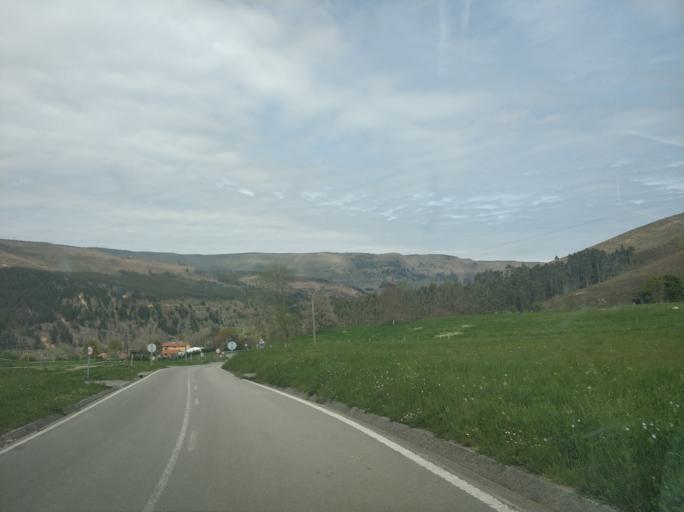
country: ES
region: Cantabria
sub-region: Provincia de Cantabria
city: Ruente
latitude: 43.2358
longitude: -4.2820
